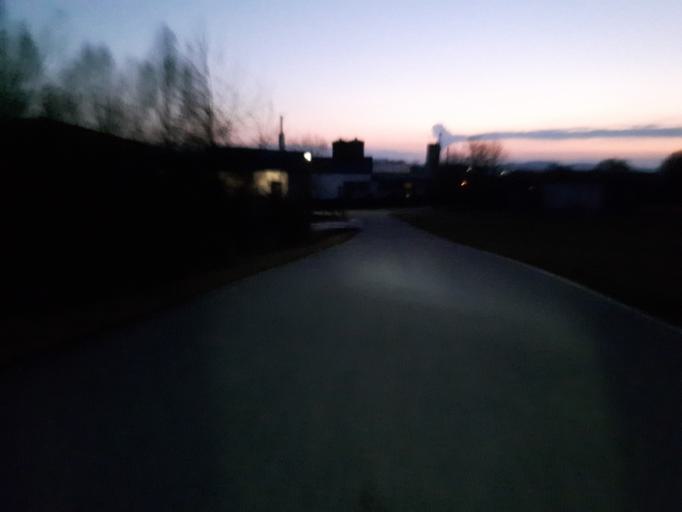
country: DE
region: Baden-Wuerttemberg
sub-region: Regierungsbezirk Stuttgart
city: Bretzfeld
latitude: 49.1420
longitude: 9.4121
